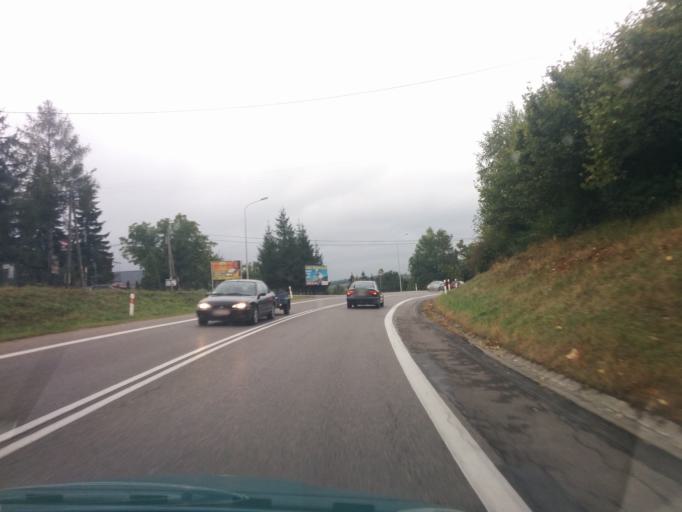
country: PL
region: Subcarpathian Voivodeship
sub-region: Powiat sanocki
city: Sanok
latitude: 49.5729
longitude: 22.1508
